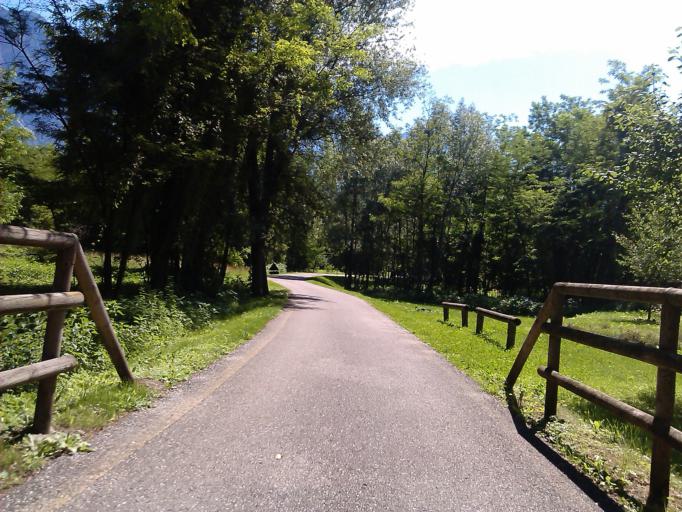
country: IT
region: Trentino-Alto Adige
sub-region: Provincia di Trento
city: Scurelle
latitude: 46.0461
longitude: 11.5091
